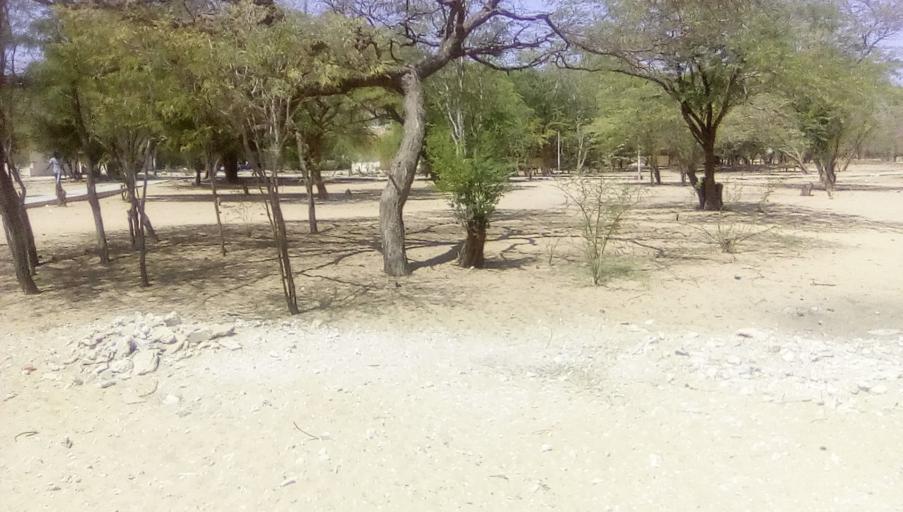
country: SN
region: Saint-Louis
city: Saint-Louis
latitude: 16.0637
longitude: -16.4217
